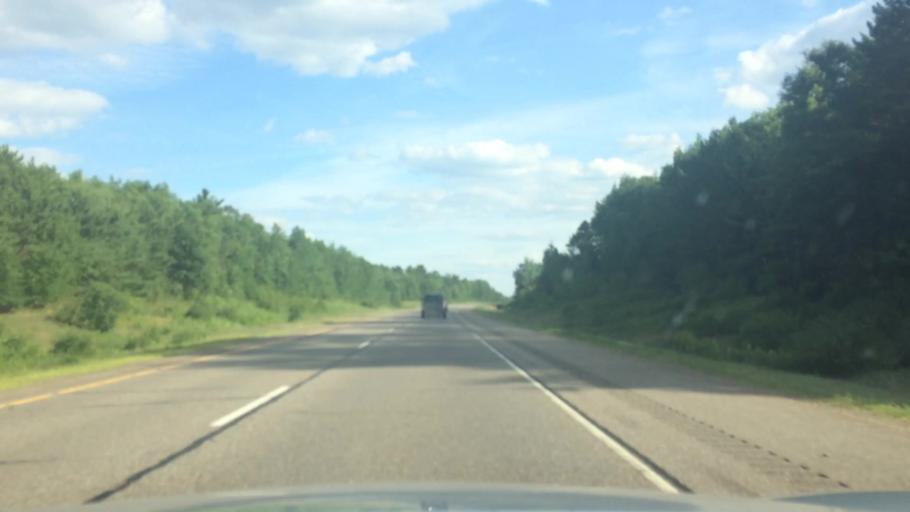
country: US
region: Wisconsin
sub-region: Lincoln County
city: Merrill
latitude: 45.1475
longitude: -89.6429
